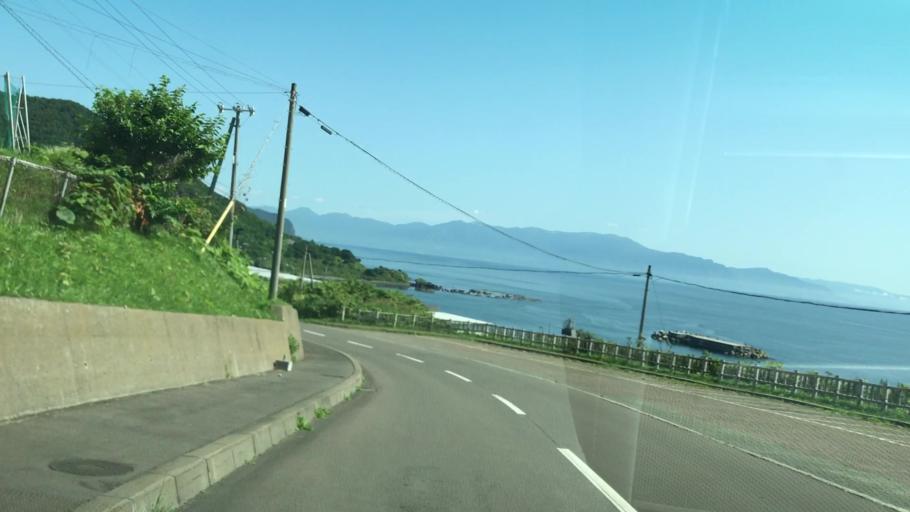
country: JP
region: Hokkaido
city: Iwanai
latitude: 43.1459
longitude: 140.4233
